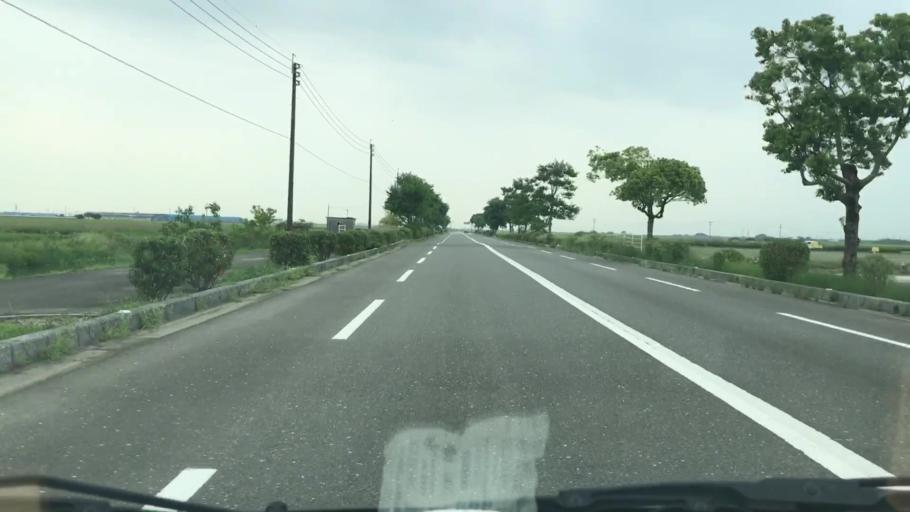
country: JP
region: Saga Prefecture
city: Okawa
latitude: 33.1859
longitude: 130.3010
